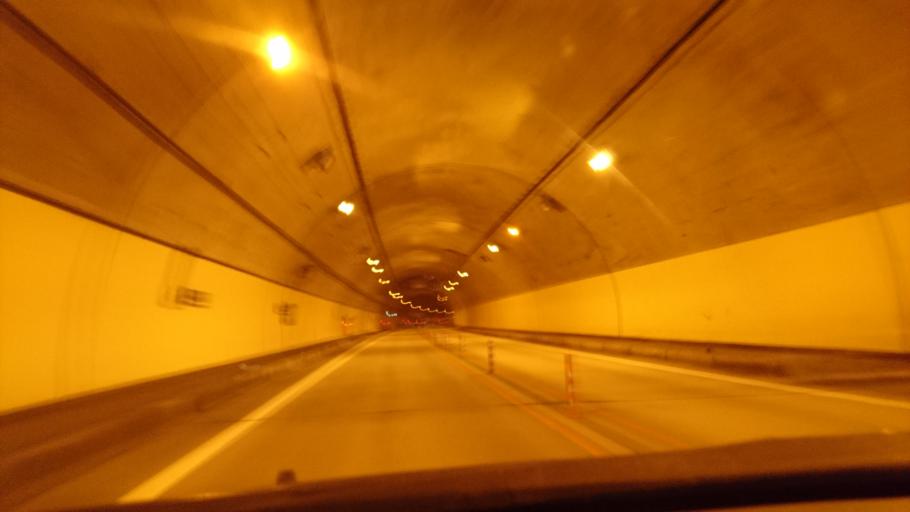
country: JP
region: Iwate
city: Kitakami
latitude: 39.2944
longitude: 141.2925
